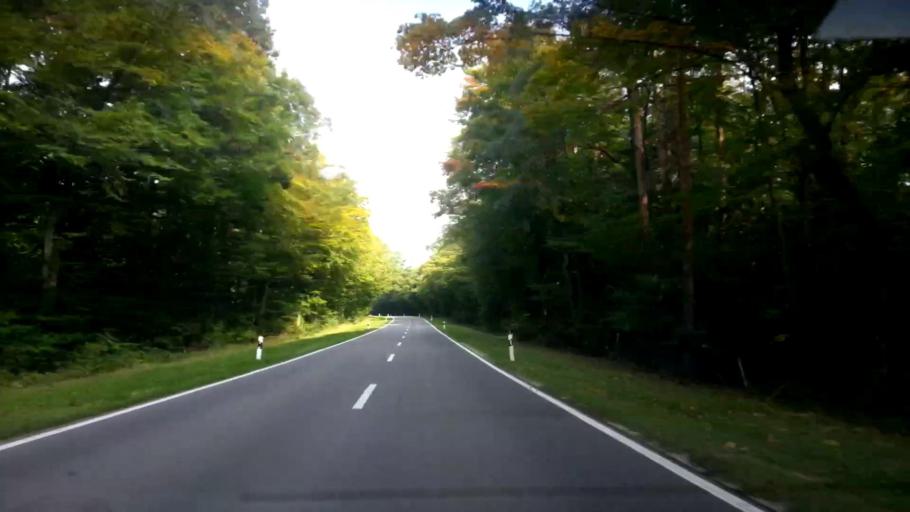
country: DE
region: Bavaria
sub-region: Regierungsbezirk Unterfranken
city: Eltmann
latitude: 49.9581
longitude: 10.6371
